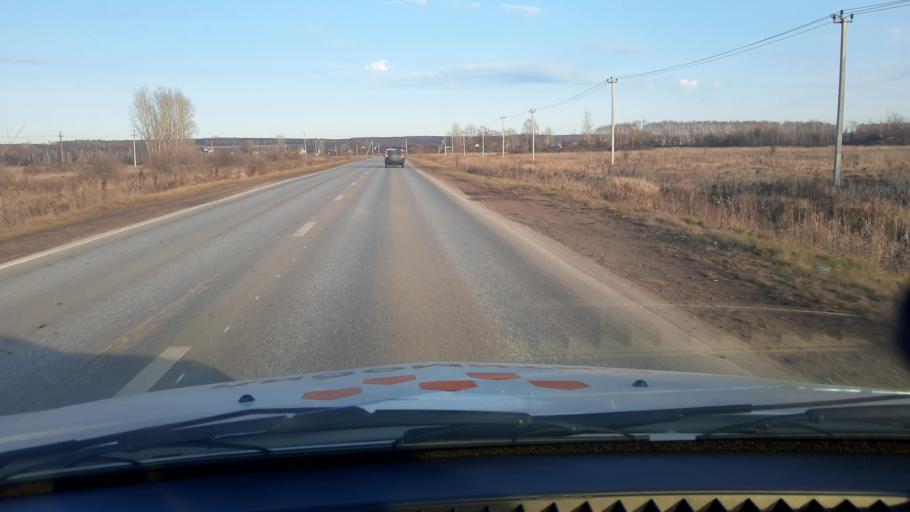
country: RU
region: Bashkortostan
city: Kabakovo
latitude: 54.6812
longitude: 56.1200
